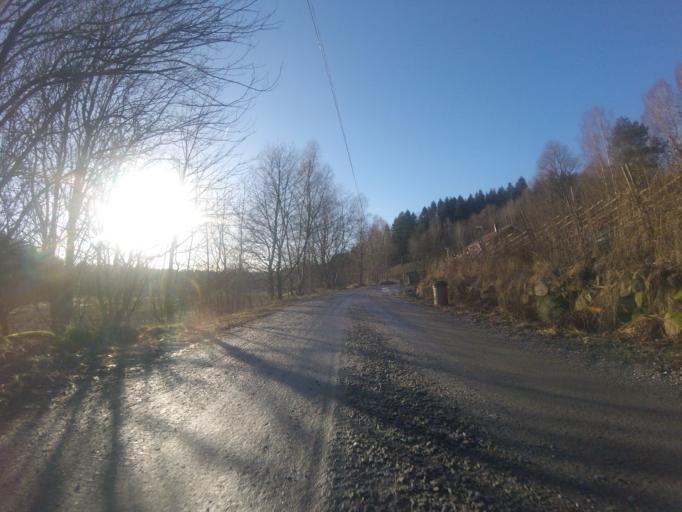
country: SE
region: Halland
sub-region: Varbergs Kommun
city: Veddige
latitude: 57.2271
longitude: 12.3000
